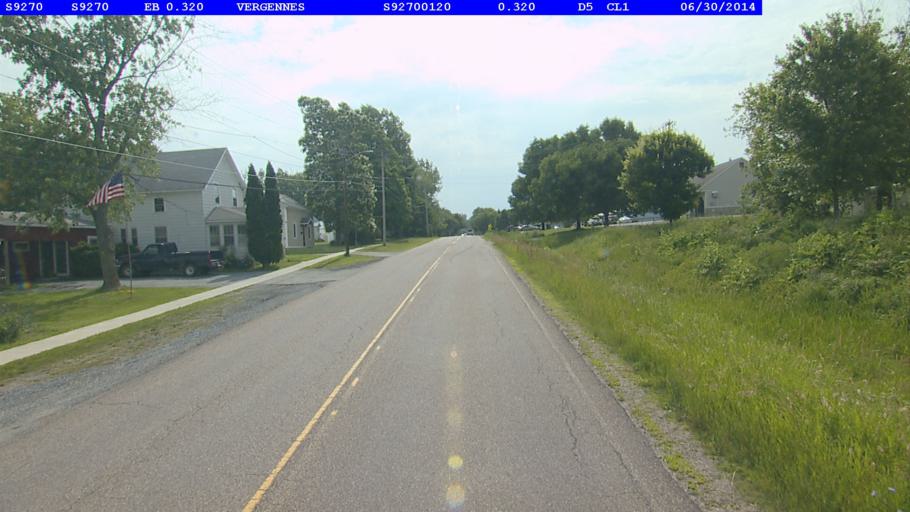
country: US
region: Vermont
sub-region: Addison County
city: Vergennes
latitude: 44.1651
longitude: -73.2470
